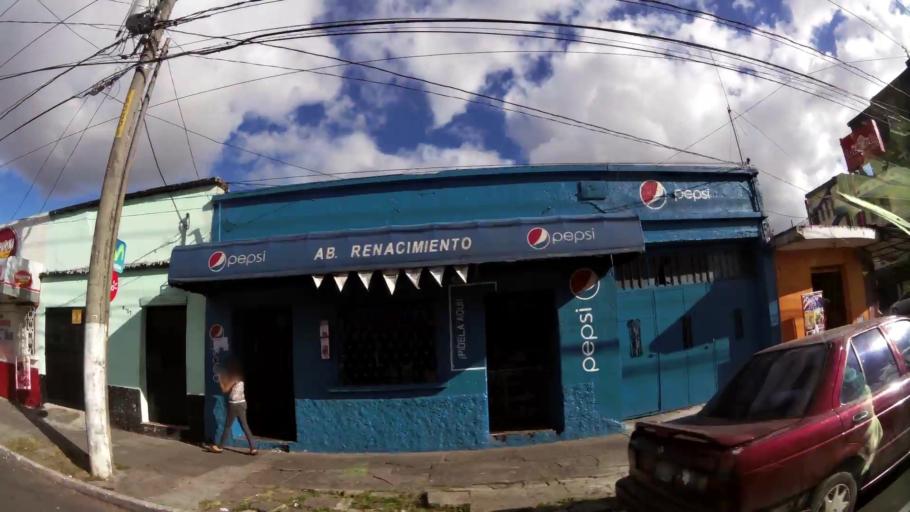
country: GT
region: Guatemala
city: Guatemala City
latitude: 14.6139
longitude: -90.5474
